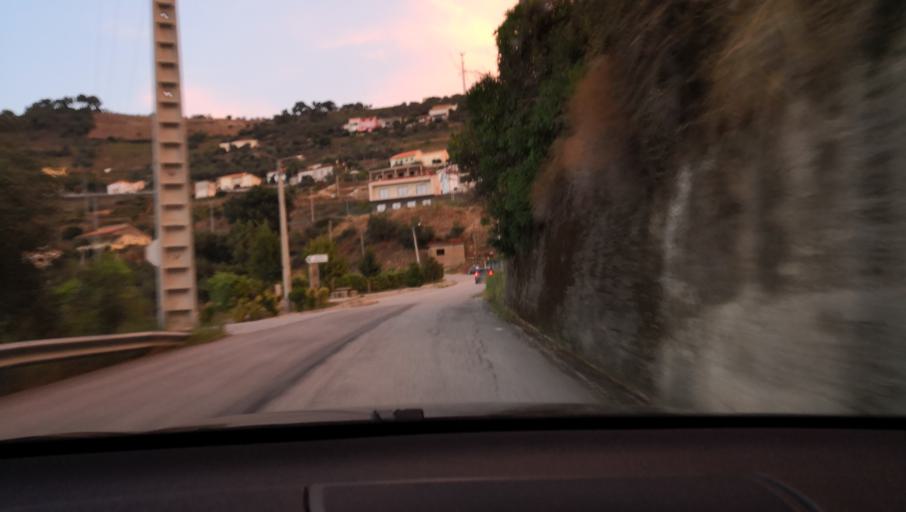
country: PT
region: Vila Real
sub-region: Santa Marta de Penaguiao
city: Santa Marta de Penaguiao
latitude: 41.2020
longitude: -7.7506
